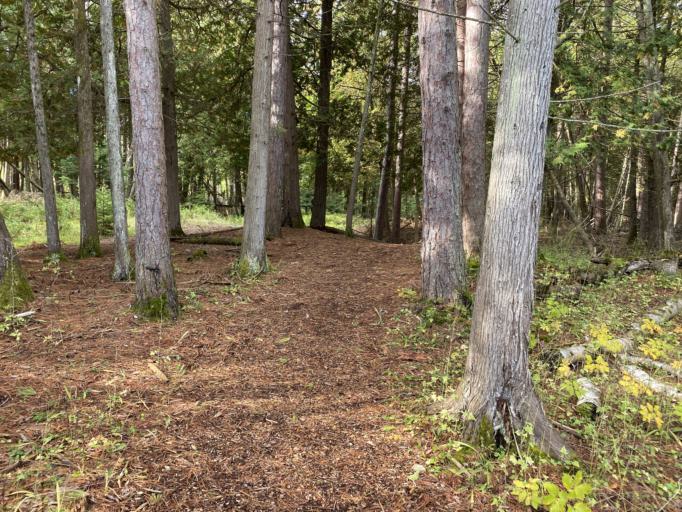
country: US
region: Michigan
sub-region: Mackinac County
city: Saint Ignace
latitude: 45.7515
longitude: -84.8806
